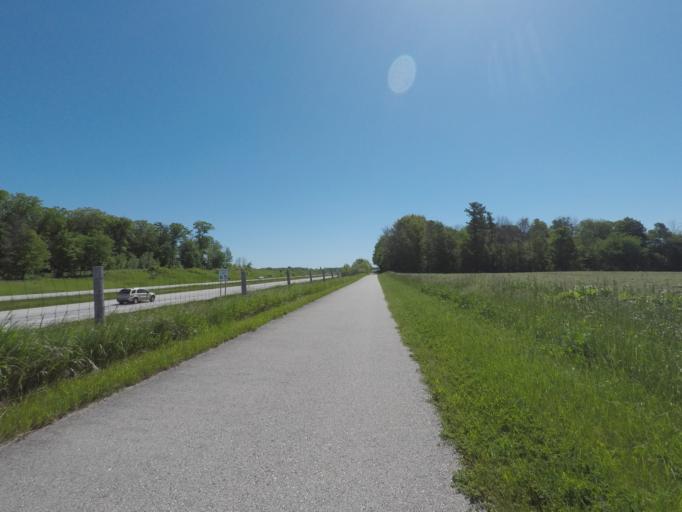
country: US
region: Wisconsin
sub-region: Sheboygan County
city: Sheboygan Falls
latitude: 43.7502
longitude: -87.8113
